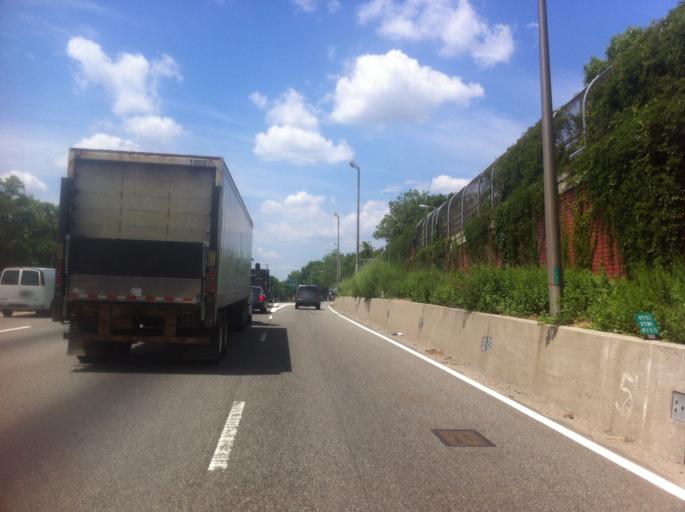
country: US
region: New York
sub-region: Nassau County
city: Lake Success
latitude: 40.7512
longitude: -73.7491
